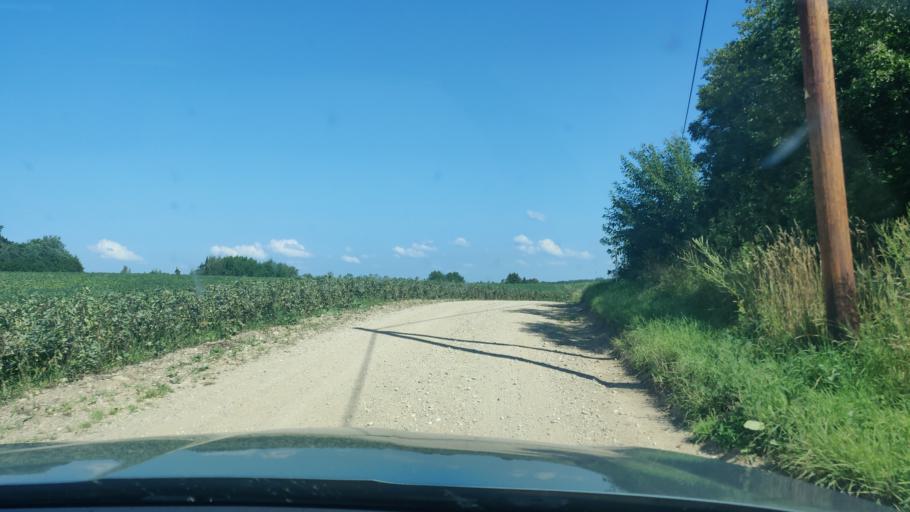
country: EE
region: Tartu
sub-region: Elva linn
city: Elva
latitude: 58.1170
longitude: 26.4598
